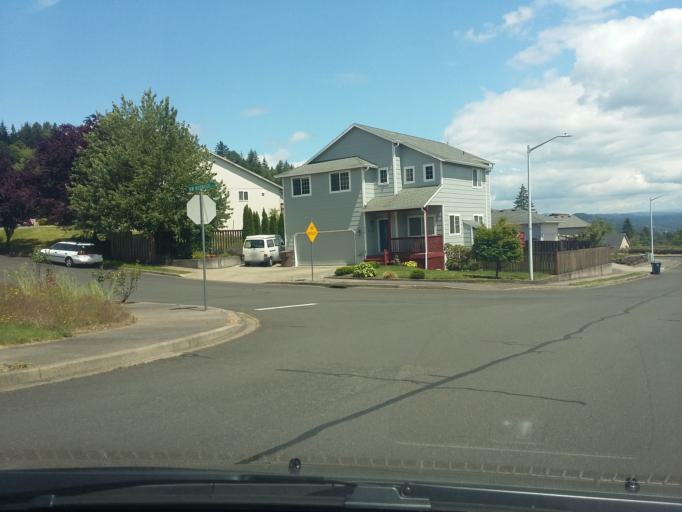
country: US
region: Washington
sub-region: Clark County
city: Camas
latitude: 45.5856
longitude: -122.4255
